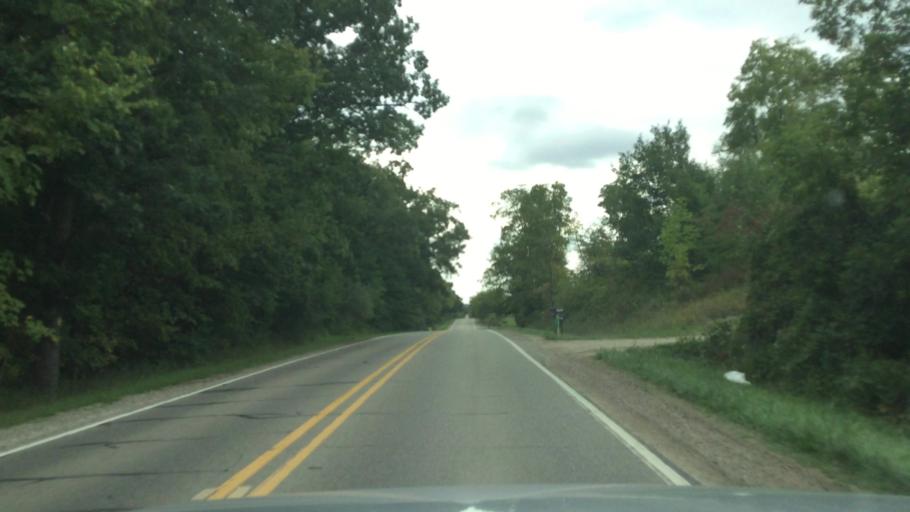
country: US
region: Michigan
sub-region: Livingston County
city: Howell
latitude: 42.6570
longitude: -83.8765
